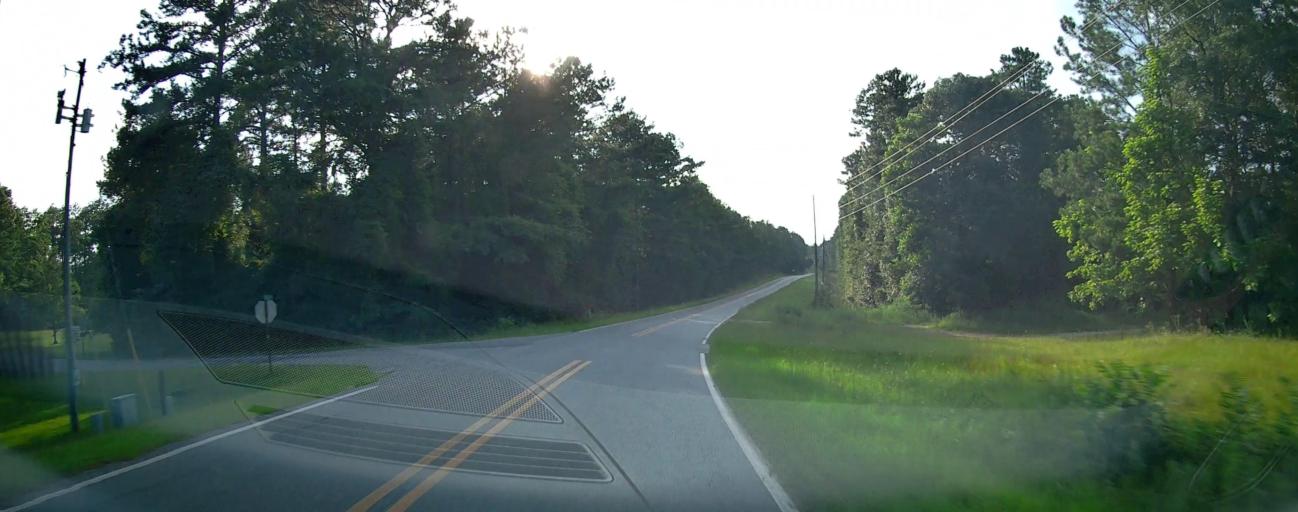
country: US
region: Georgia
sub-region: Peach County
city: Byron
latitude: 32.7056
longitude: -83.8327
